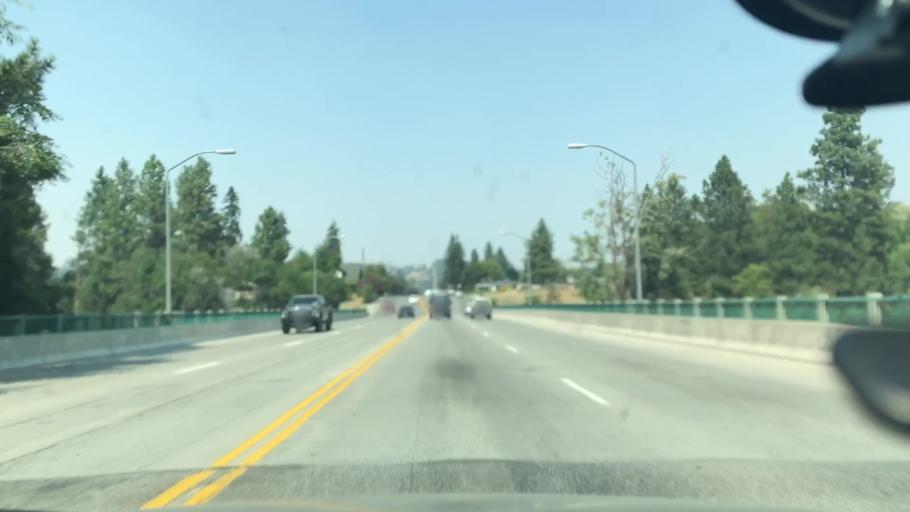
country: US
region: Washington
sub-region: Spokane County
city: Millwood
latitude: 47.6894
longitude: -117.2827
